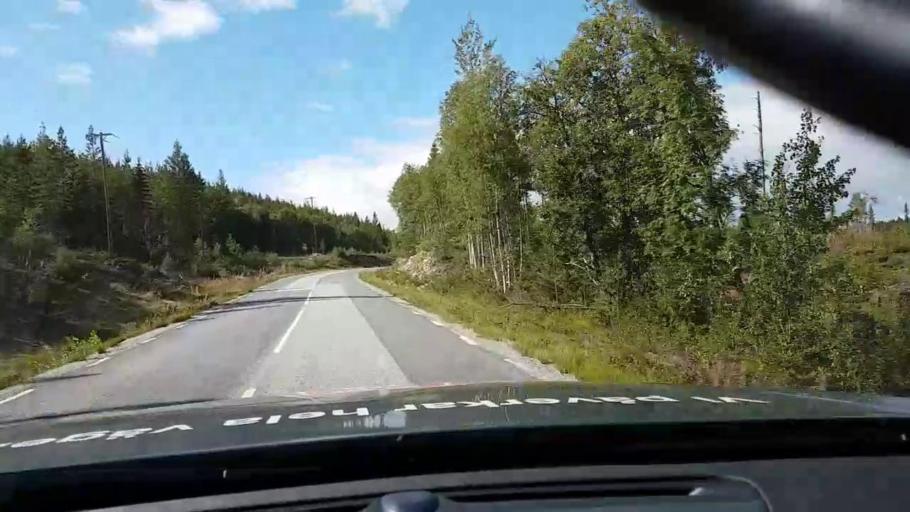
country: SE
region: Vaesterbotten
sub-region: Asele Kommun
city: Asele
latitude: 63.8296
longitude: 17.4582
